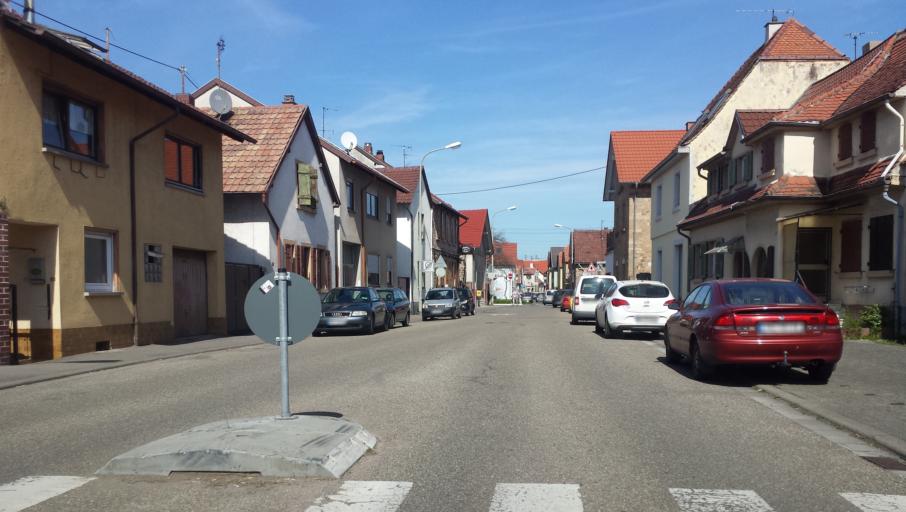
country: DE
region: Rheinland-Pfalz
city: Neustadt
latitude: 49.3663
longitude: 8.1728
